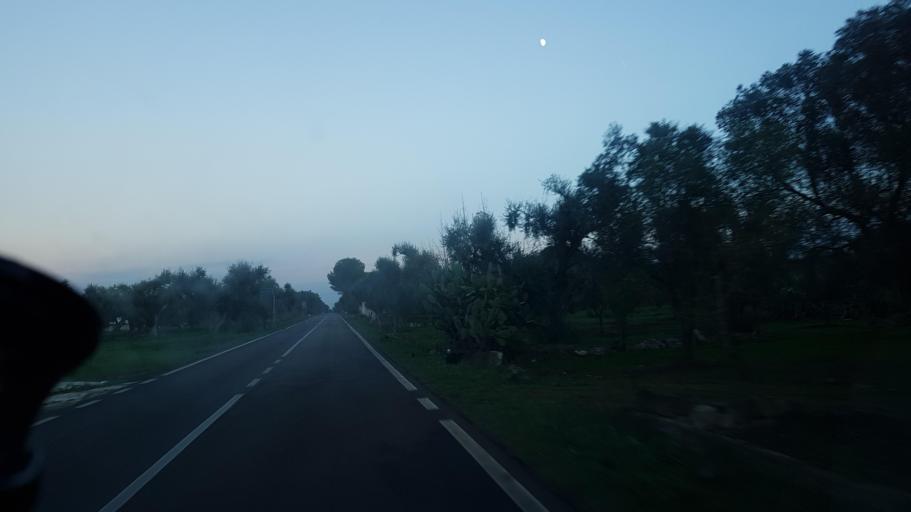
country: IT
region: Apulia
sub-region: Provincia di Brindisi
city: Latiano
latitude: 40.5694
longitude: 17.6675
